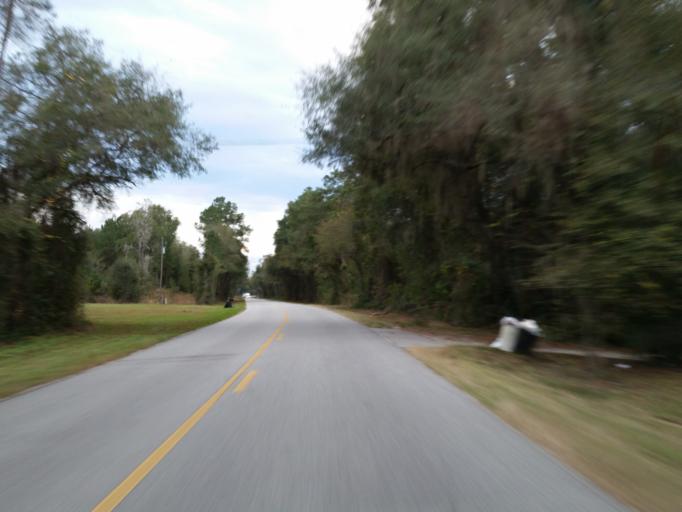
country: US
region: Florida
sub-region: Hamilton County
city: Jasper
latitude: 30.5613
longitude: -83.0989
